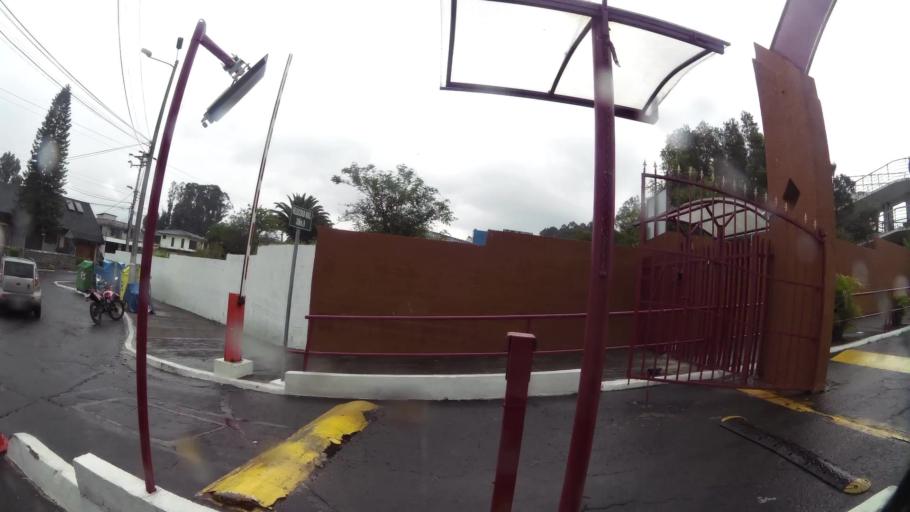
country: EC
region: Pichincha
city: Sangolqui
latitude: -0.3152
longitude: -78.4417
